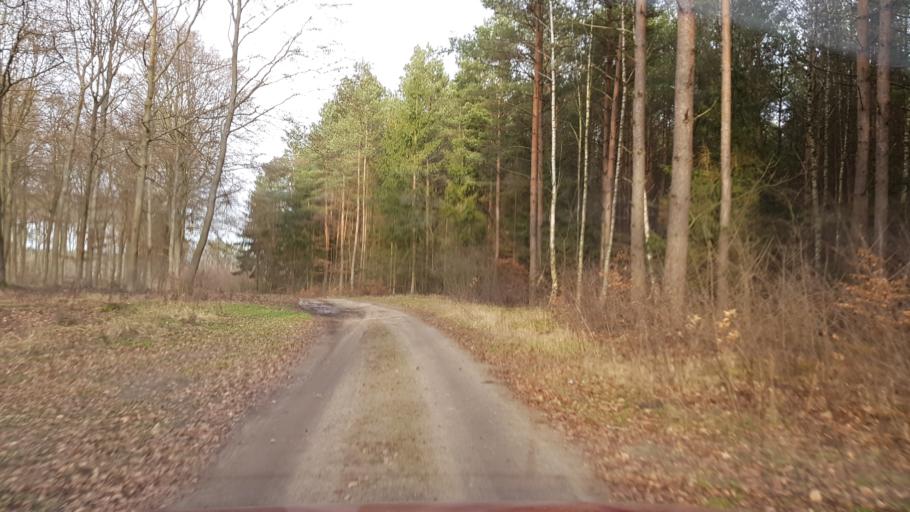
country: PL
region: Lubusz
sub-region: Powiat strzelecko-drezdenecki
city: Strzelce Krajenskie
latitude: 52.9148
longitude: 15.4118
